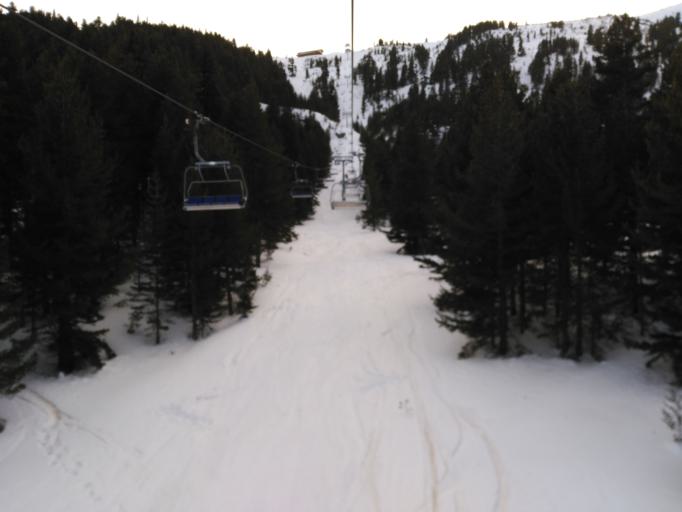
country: BG
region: Blagoevgrad
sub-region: Obshtina Bansko
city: Bansko
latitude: 41.7684
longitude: 23.4483
